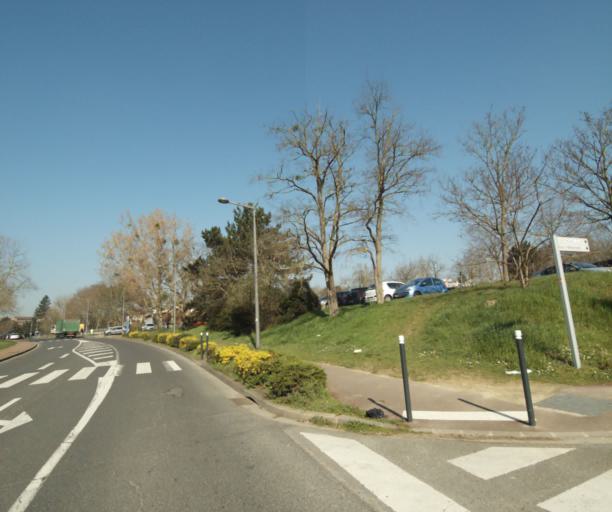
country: FR
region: Ile-de-France
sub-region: Departement du Val-d'Oise
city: Cergy
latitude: 49.0329
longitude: 2.0737
